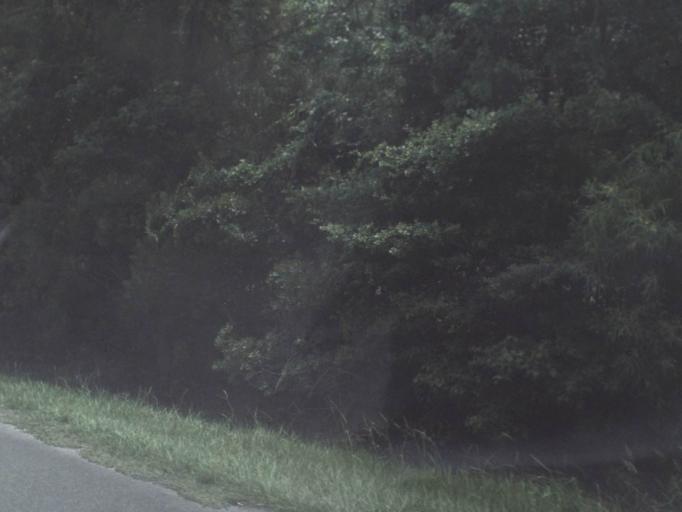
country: US
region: Florida
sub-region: Nassau County
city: Nassau Village-Ratliff
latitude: 30.4793
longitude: -81.7160
